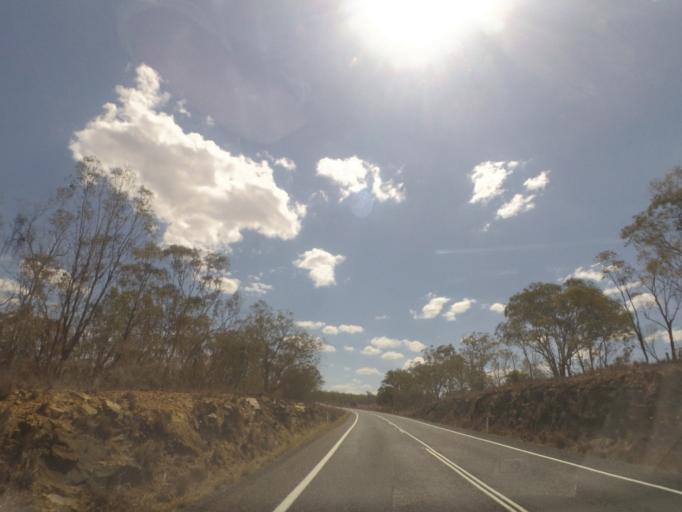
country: AU
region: Queensland
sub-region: Southern Downs
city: Warwick
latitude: -28.1608
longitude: 151.6907
